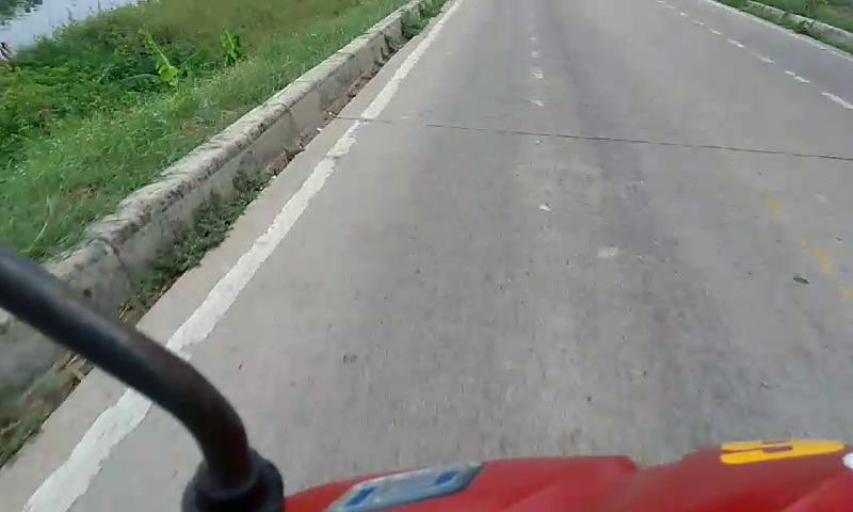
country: ID
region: West Java
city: Bekasi
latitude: -6.1476
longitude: 106.9703
